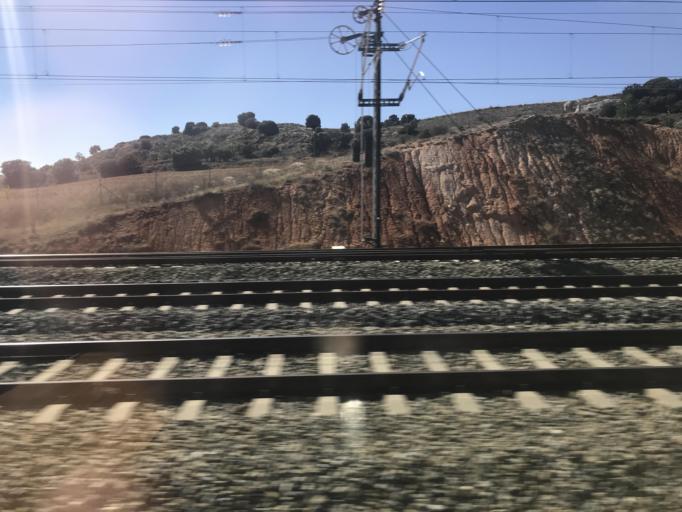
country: ES
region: Castille-La Mancha
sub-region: Provincia de Cuenca
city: Cuenca
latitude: 40.0316
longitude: -2.1402
